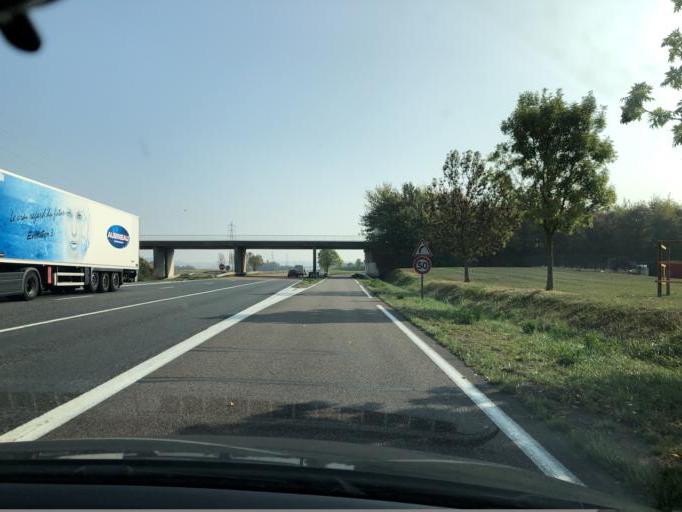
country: FR
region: Bourgogne
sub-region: Departement de l'Yonne
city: Saint-Clement
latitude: 48.2244
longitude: 3.2868
